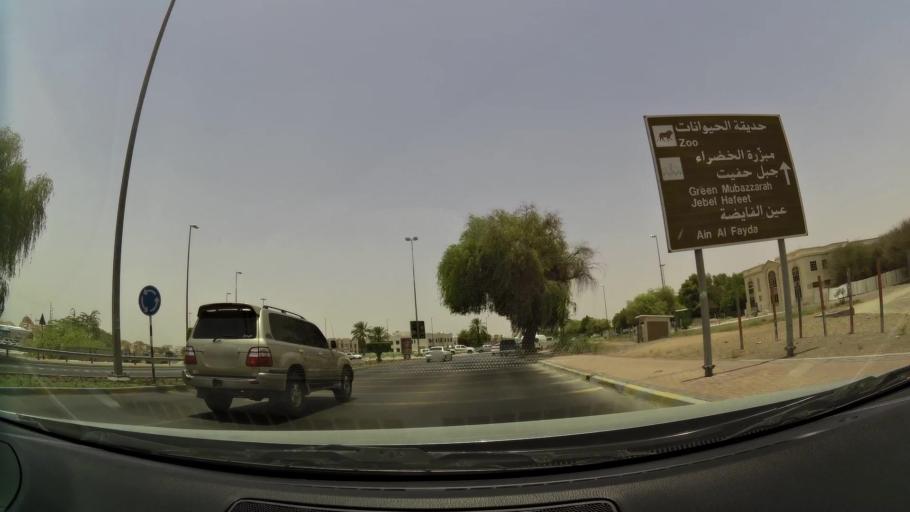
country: AE
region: Abu Dhabi
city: Al Ain
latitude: 24.2051
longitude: 55.7481
